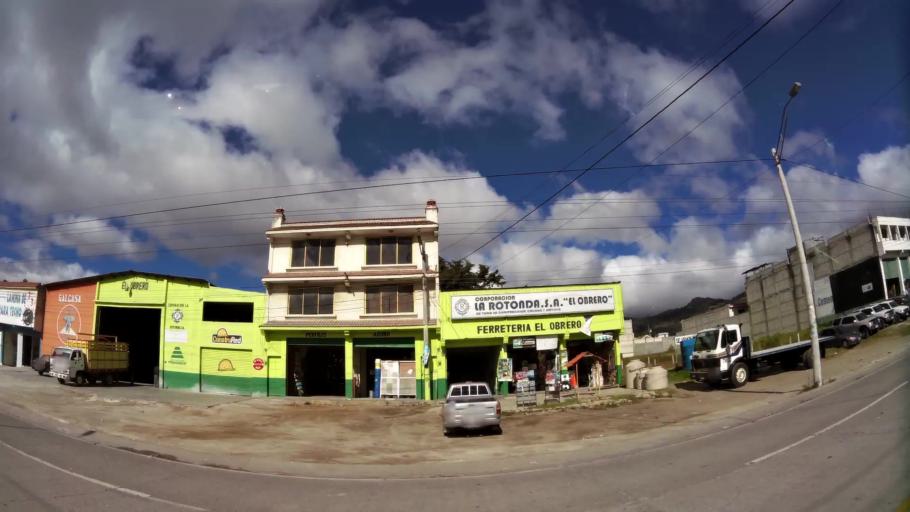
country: GT
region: Quetzaltenango
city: Salcaja
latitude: 14.8913
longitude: -91.4562
